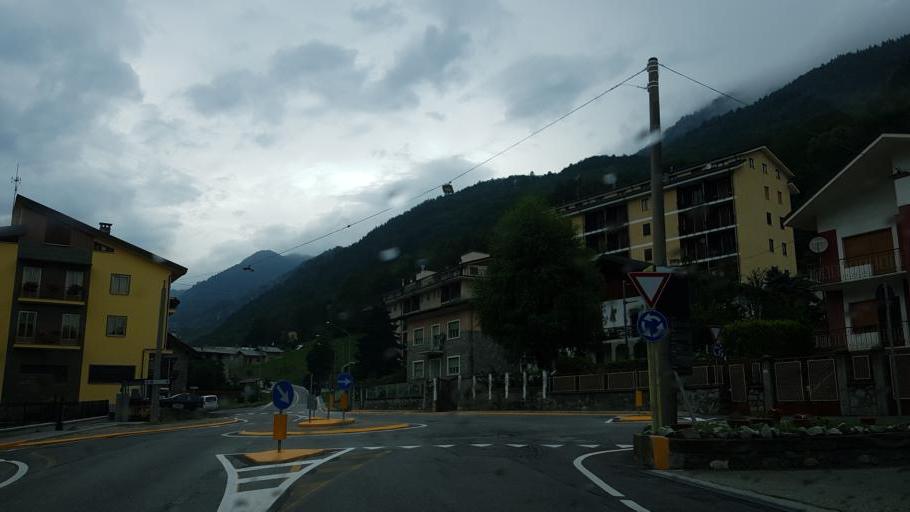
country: IT
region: Piedmont
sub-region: Provincia di Cuneo
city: Sampeyre
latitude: 44.5798
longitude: 7.1827
